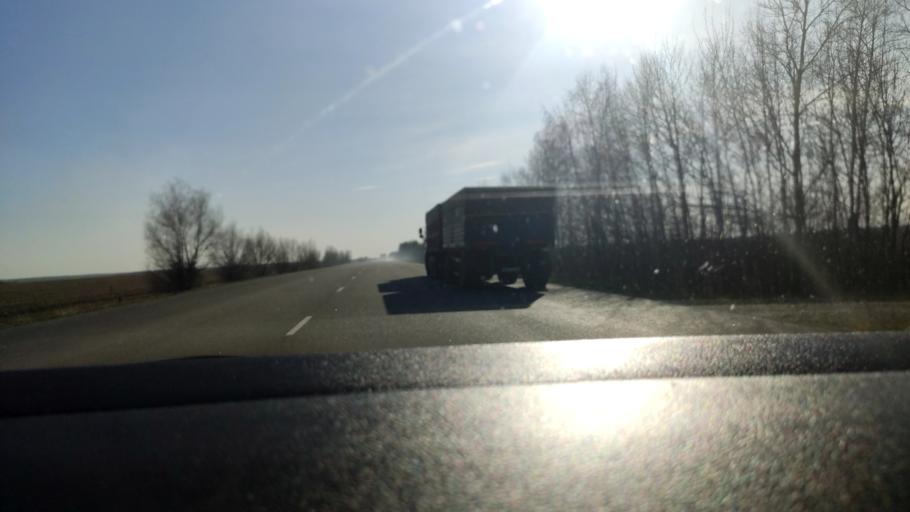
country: RU
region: Voronezj
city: Kolodeznyy
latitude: 51.3269
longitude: 39.1278
